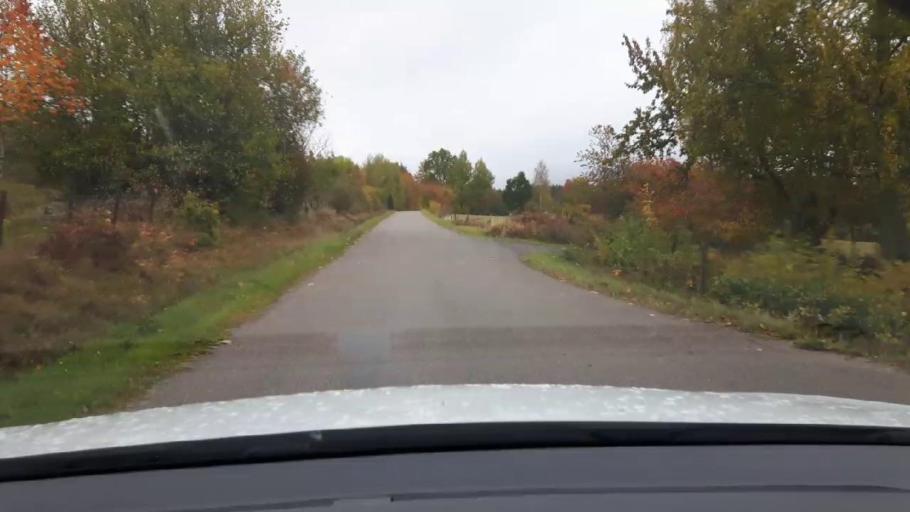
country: SE
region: Kalmar
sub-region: Vimmerby Kommun
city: Sodra Vi
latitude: 57.9565
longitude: 15.9014
